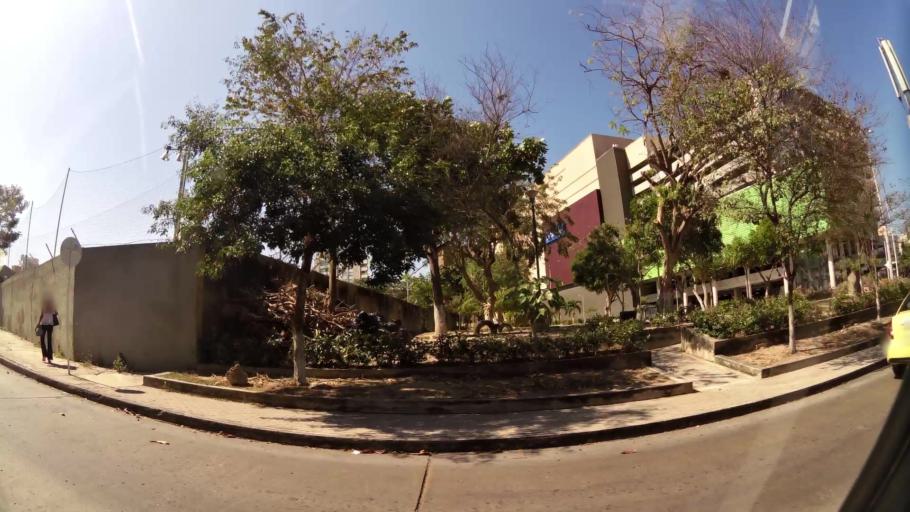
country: CO
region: Atlantico
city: Barranquilla
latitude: 11.0105
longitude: -74.8192
